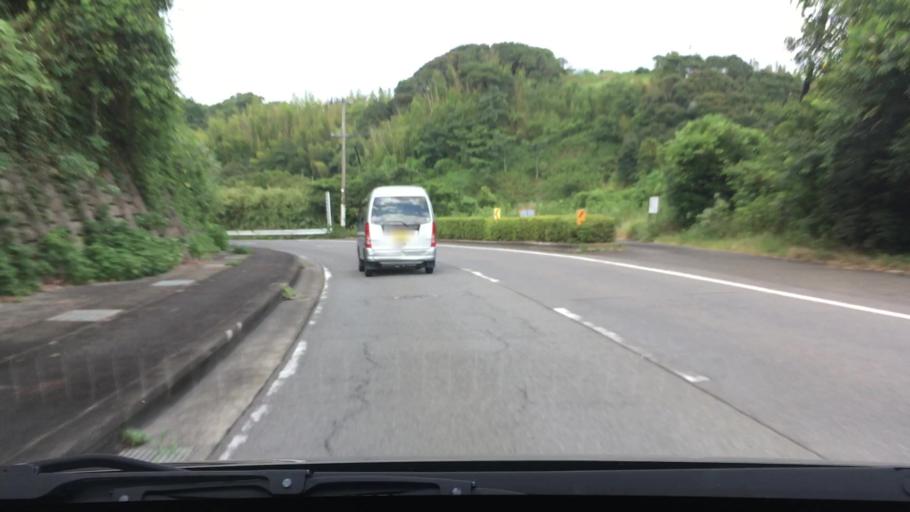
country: JP
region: Nagasaki
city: Togitsu
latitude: 32.8195
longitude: 129.7401
